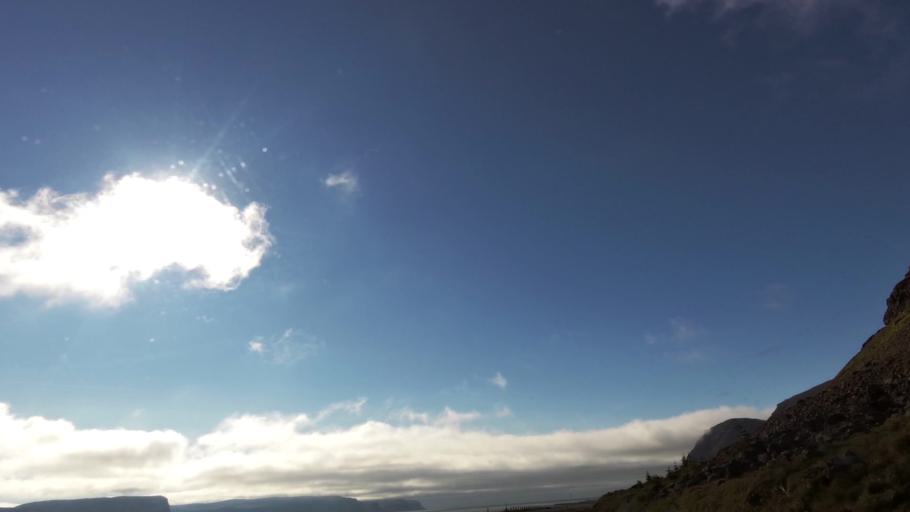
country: IS
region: West
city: Olafsvik
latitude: 65.5820
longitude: -23.9614
